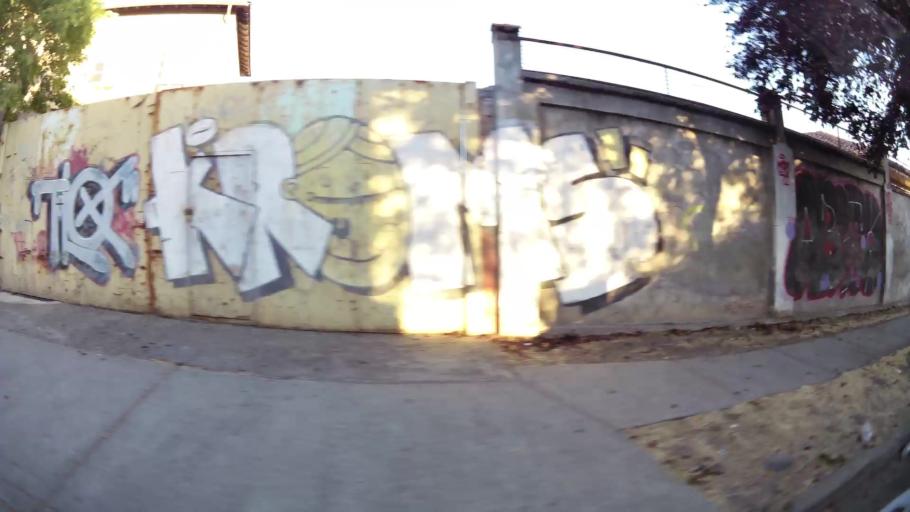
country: CL
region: O'Higgins
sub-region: Provincia de Cachapoal
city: Rancagua
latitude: -34.1685
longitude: -70.7556
